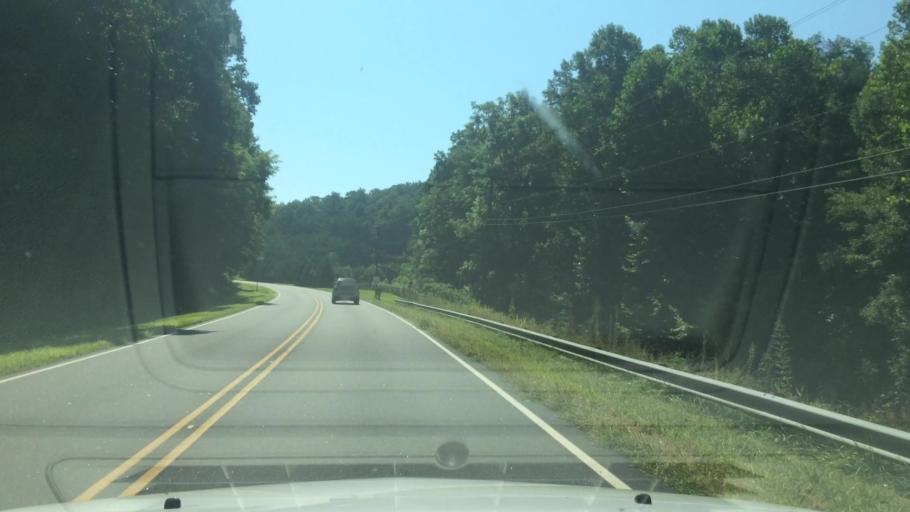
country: US
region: North Carolina
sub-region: Caldwell County
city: Lenoir
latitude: 35.9149
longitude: -81.4818
